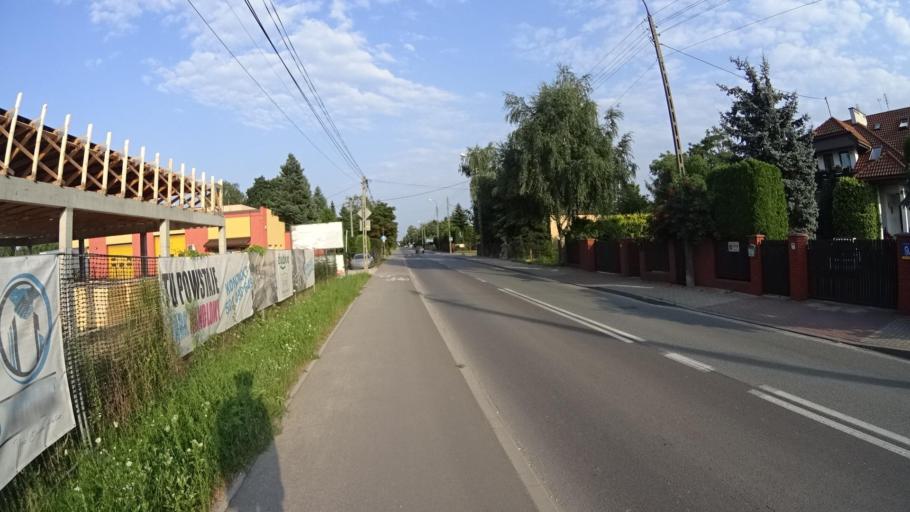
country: PL
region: Masovian Voivodeship
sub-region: Powiat pruszkowski
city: Rybie
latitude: 52.1484
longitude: 20.9414
